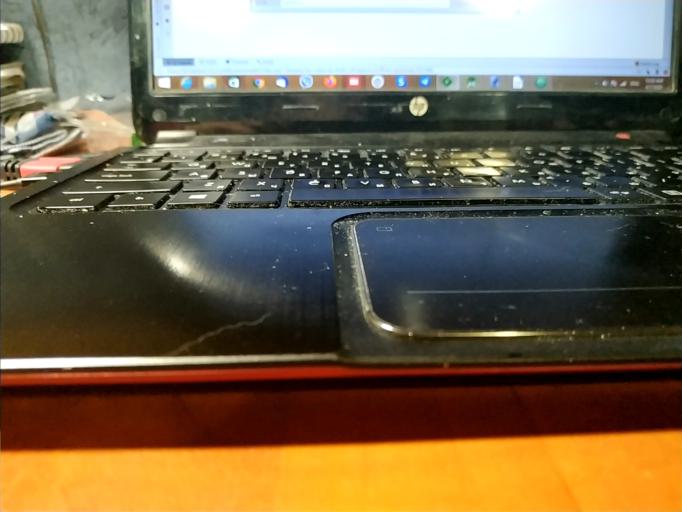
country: RU
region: Vologda
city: Suda
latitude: 58.9169
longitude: 37.5432
